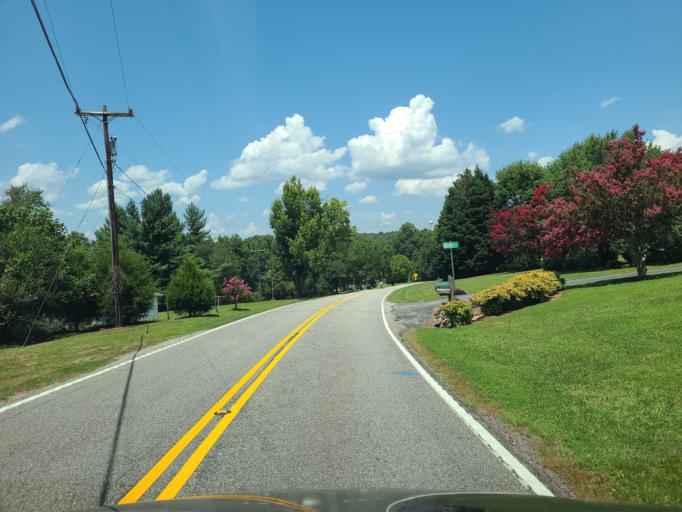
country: US
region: South Carolina
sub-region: Spartanburg County
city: Duncan
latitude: 34.9734
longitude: -82.1761
